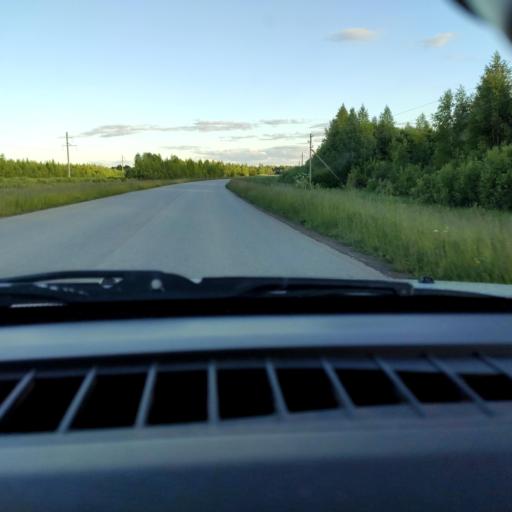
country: RU
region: Perm
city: Polazna
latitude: 58.2053
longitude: 56.5308
